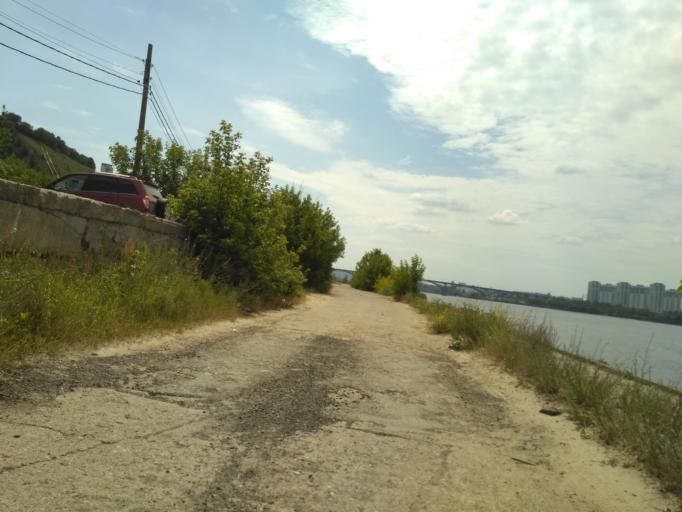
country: RU
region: Nizjnij Novgorod
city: Nizhniy Novgorod
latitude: 56.3149
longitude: 43.9690
